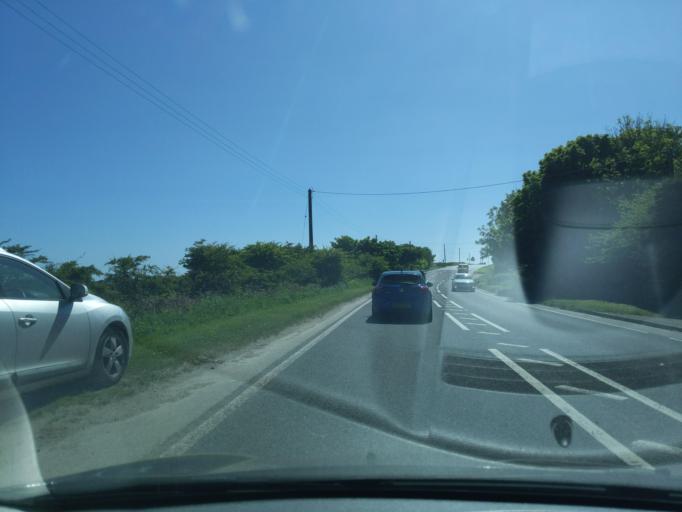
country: GB
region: England
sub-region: Cornwall
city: Wendron
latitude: 50.1536
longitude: -5.1932
